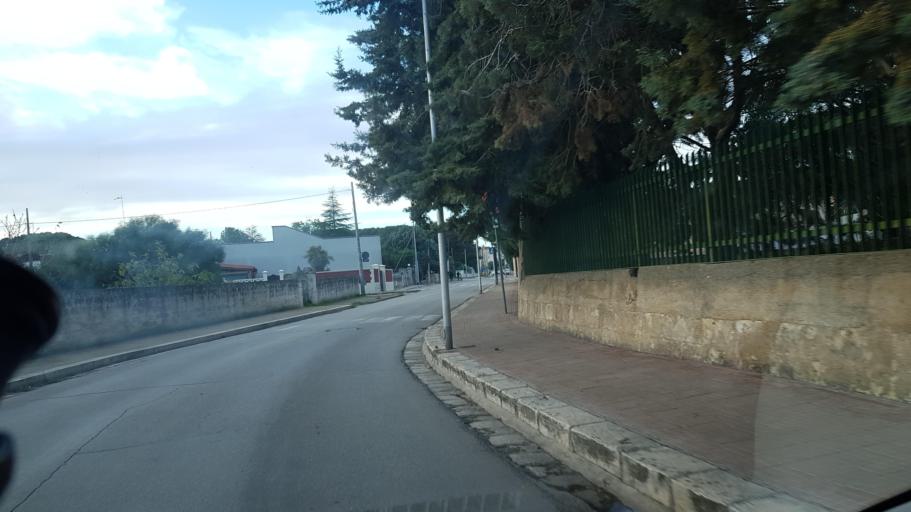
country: IT
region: Apulia
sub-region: Provincia di Brindisi
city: San Vito dei Normanni
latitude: 40.6601
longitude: 17.6991
